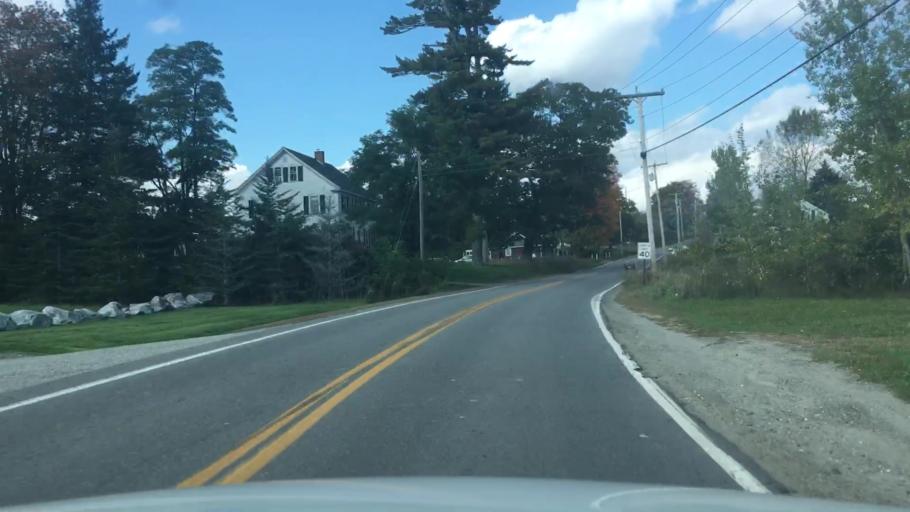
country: US
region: Maine
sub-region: Knox County
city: Union
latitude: 44.2183
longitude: -69.2843
